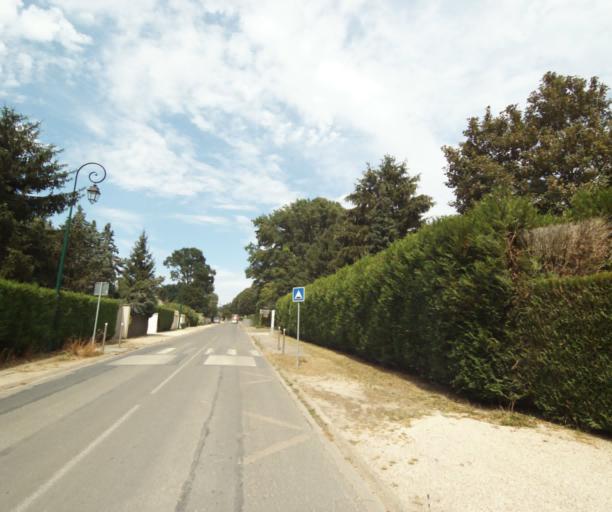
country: FR
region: Ile-de-France
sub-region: Departement de Seine-et-Marne
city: Barbizon
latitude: 48.4427
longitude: 2.5988
